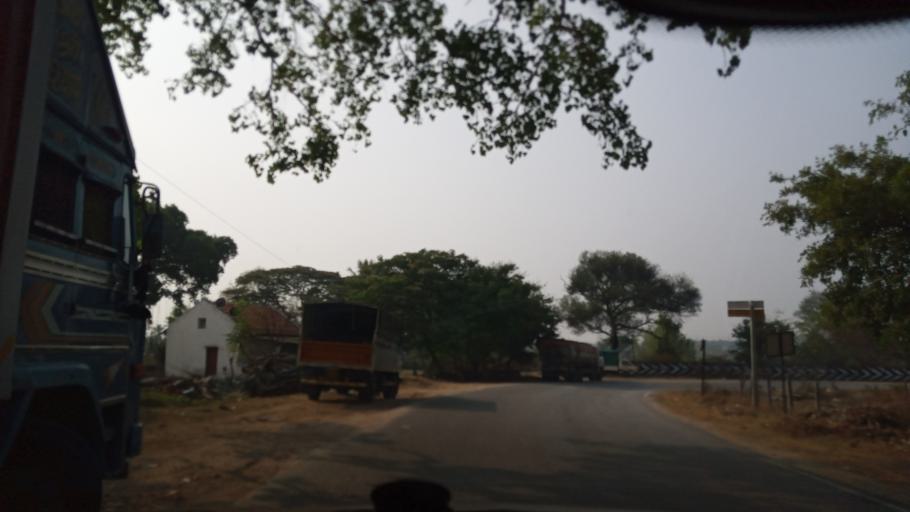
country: IN
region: Karnataka
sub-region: Mandya
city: Belluru
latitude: 12.9627
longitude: 76.7629
